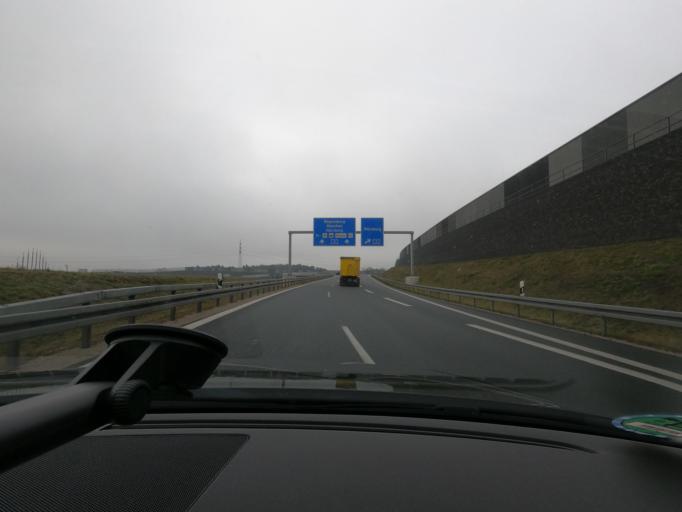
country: DE
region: Bavaria
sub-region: Regierungsbezirk Mittelfranken
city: Erlangen
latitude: 49.5620
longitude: 10.9908
